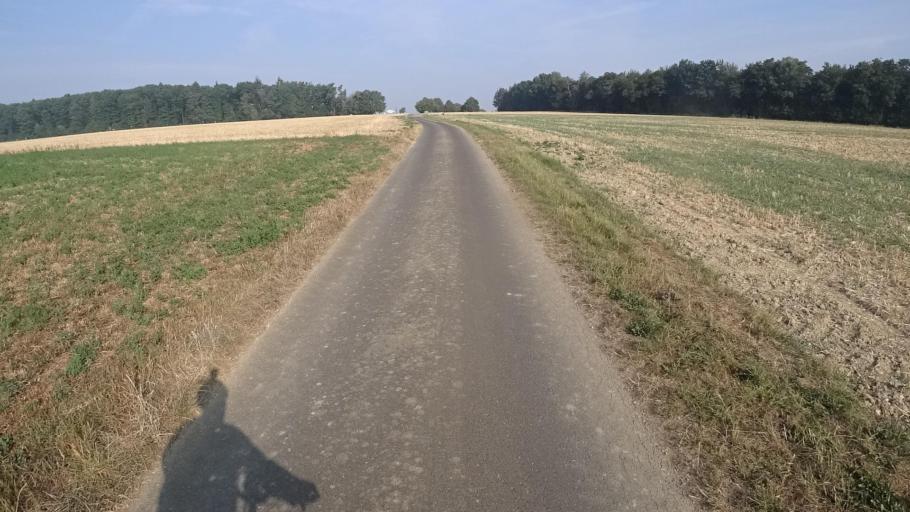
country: DE
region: Rheinland-Pfalz
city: Holzbach
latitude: 49.9466
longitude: 7.5413
